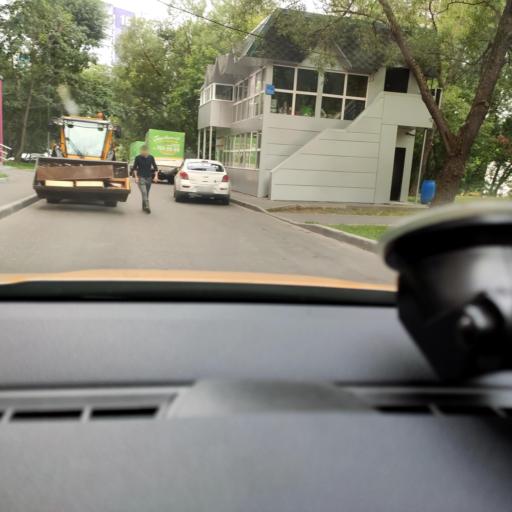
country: RU
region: Moskovskaya
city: Alekseyevka
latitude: 55.6332
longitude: 37.7962
